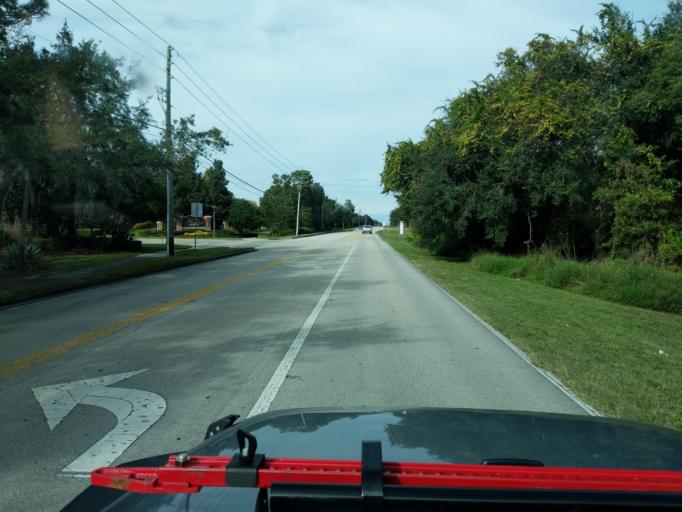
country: US
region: Florida
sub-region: Orange County
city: Lake Butler
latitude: 28.5203
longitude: -81.5416
